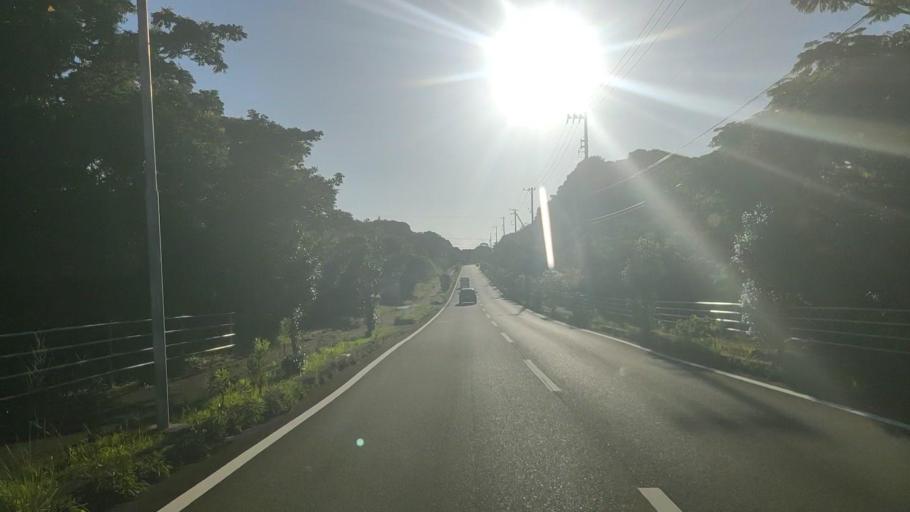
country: JP
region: Mie
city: Toba
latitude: 34.2635
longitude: 136.8209
